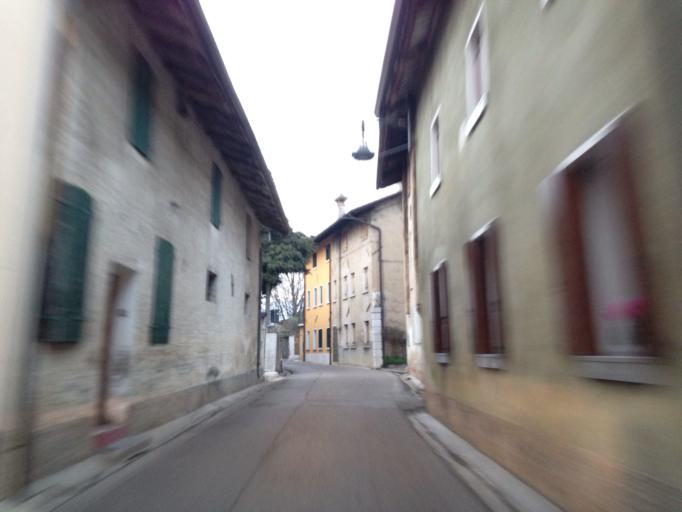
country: IT
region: Friuli Venezia Giulia
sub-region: Provincia di Pordenone
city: Cavolano-Schiavoi
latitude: 45.9446
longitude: 12.4919
